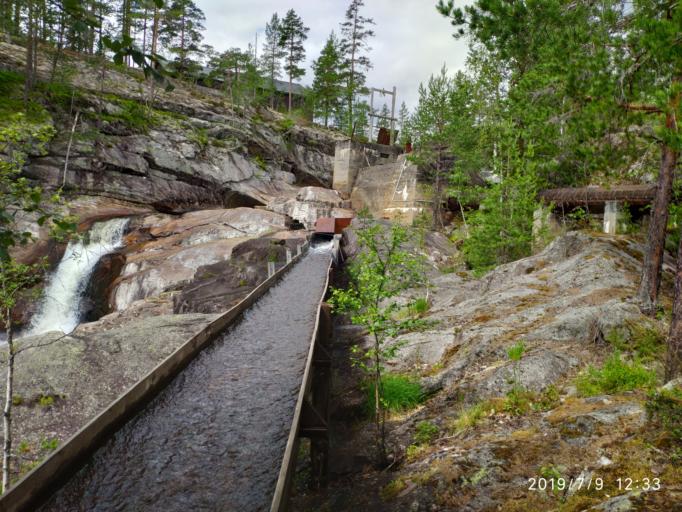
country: NO
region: Buskerud
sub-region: Fla
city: Fla
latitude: 60.2304
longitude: 9.3611
